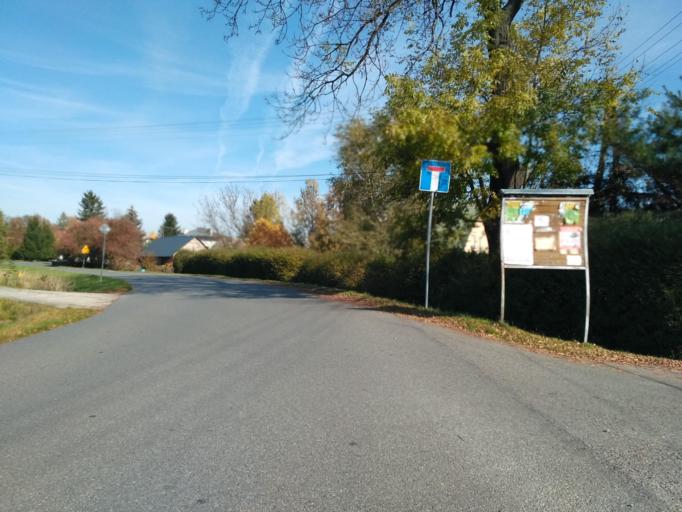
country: PL
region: Subcarpathian Voivodeship
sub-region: Powiat rzeszowski
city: Trzciana
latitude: 50.0760
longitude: 21.8002
